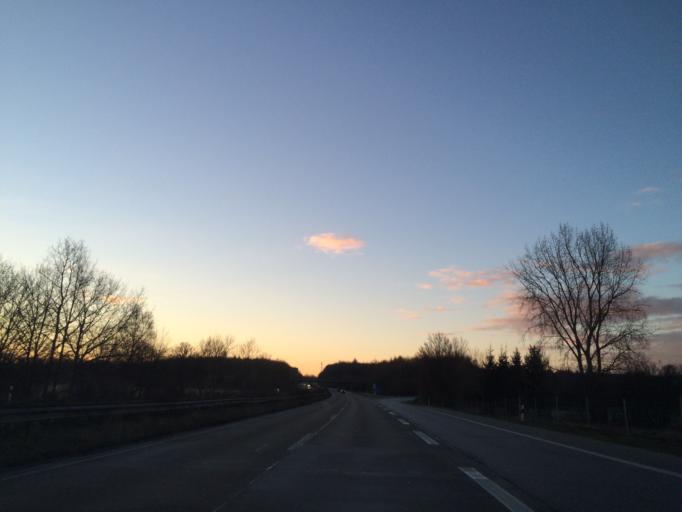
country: DE
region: Schleswig-Holstein
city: Scharbeutz
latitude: 54.0389
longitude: 10.7282
